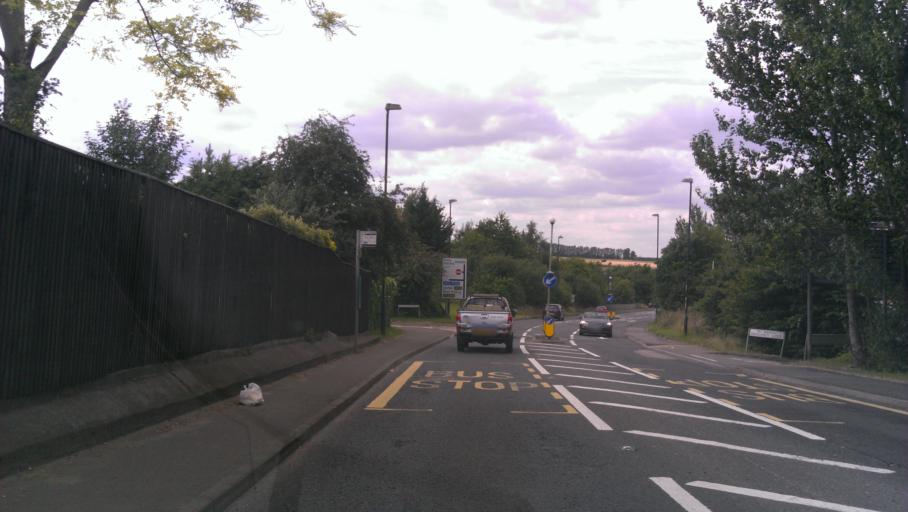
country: GB
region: England
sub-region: Kent
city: Strood
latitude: 51.4094
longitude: 0.4978
